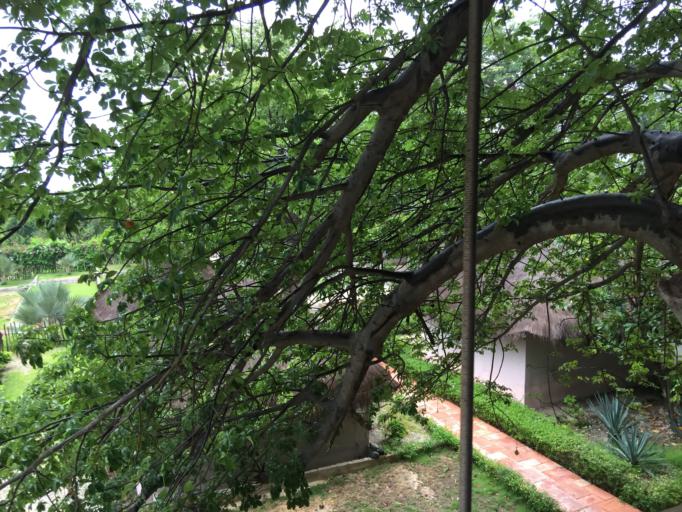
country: SN
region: Fatick
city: Sokone
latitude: 13.7845
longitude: -16.4777
